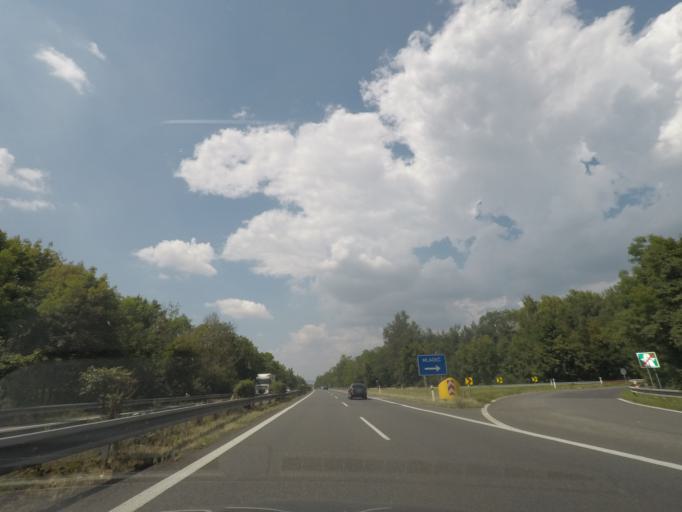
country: CZ
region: Olomoucky
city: Bila Lhota
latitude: 49.7115
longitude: 17.0192
